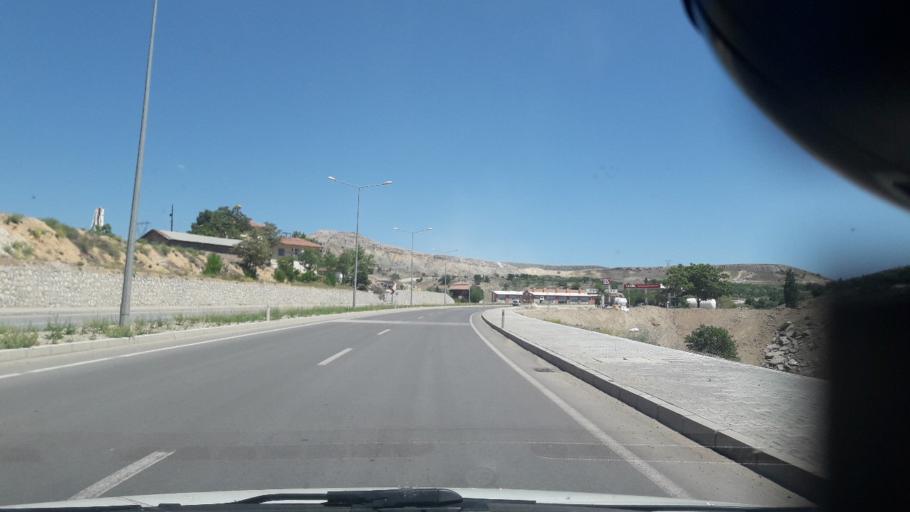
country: TR
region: Malatya
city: Hekimhan
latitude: 38.8184
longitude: 37.9409
